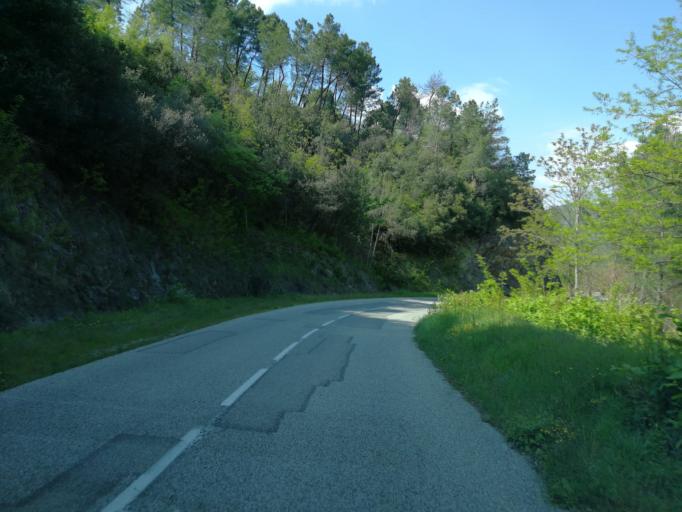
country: FR
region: Rhone-Alpes
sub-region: Departement de l'Ardeche
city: Saint-Sauveur-de-Montagut
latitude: 44.7964
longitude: 4.6146
